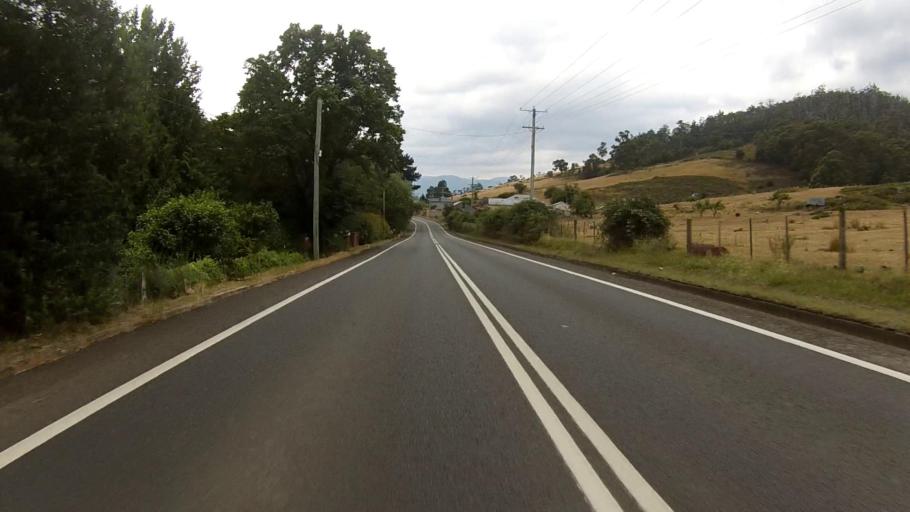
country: AU
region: Tasmania
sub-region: Huon Valley
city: Huonville
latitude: -43.0502
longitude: 147.0502
